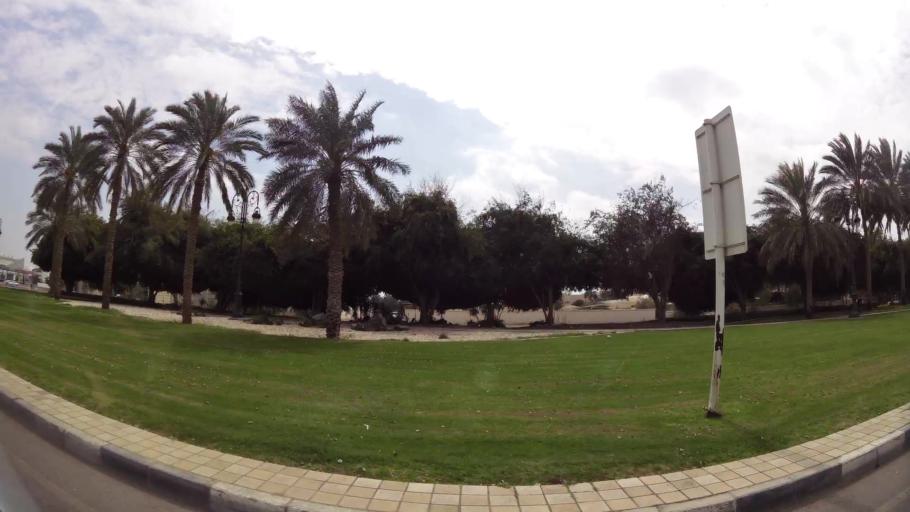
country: AE
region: Abu Dhabi
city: Al Ain
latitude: 24.2057
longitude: 55.7909
